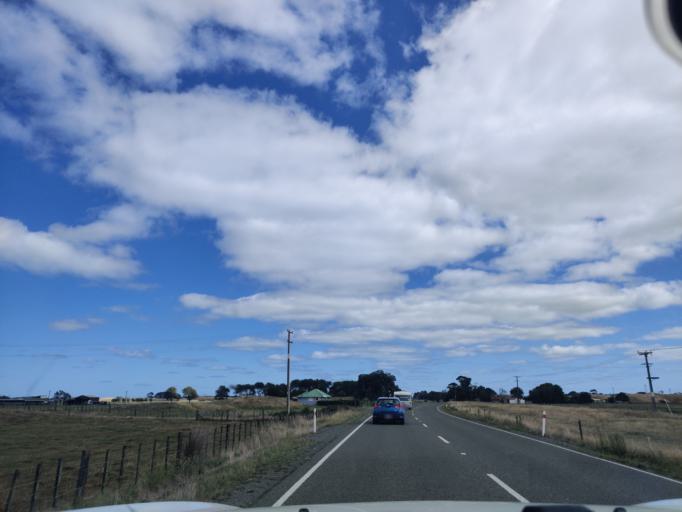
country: NZ
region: Manawatu-Wanganui
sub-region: Horowhenua District
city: Foxton
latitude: -40.4153
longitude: 175.4019
